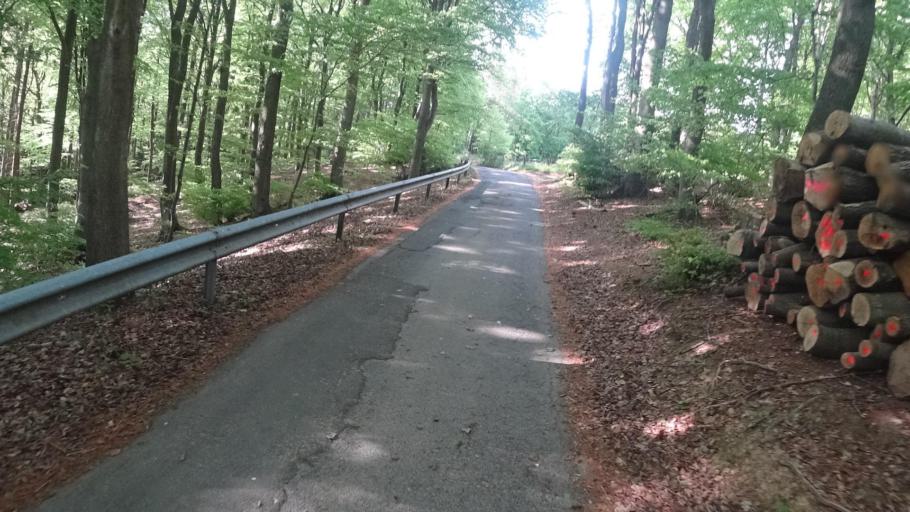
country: DE
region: Rheinland-Pfalz
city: Kirchsahr
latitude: 50.5095
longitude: 6.8699
